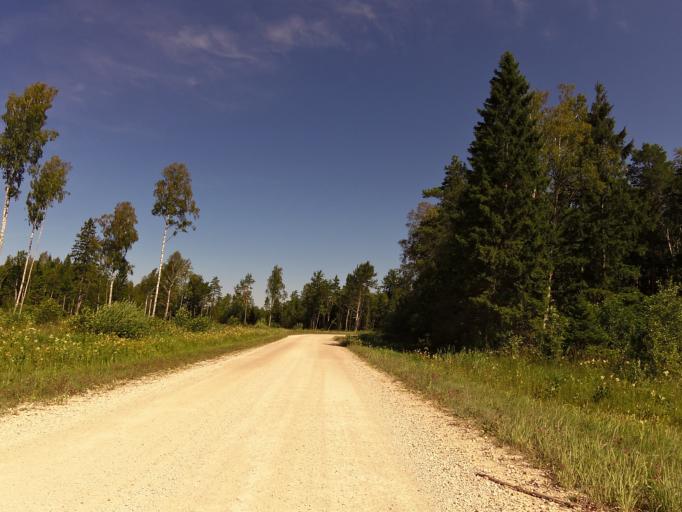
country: EE
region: Hiiumaa
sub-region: Kaerdla linn
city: Kardla
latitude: 58.9273
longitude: 22.3695
